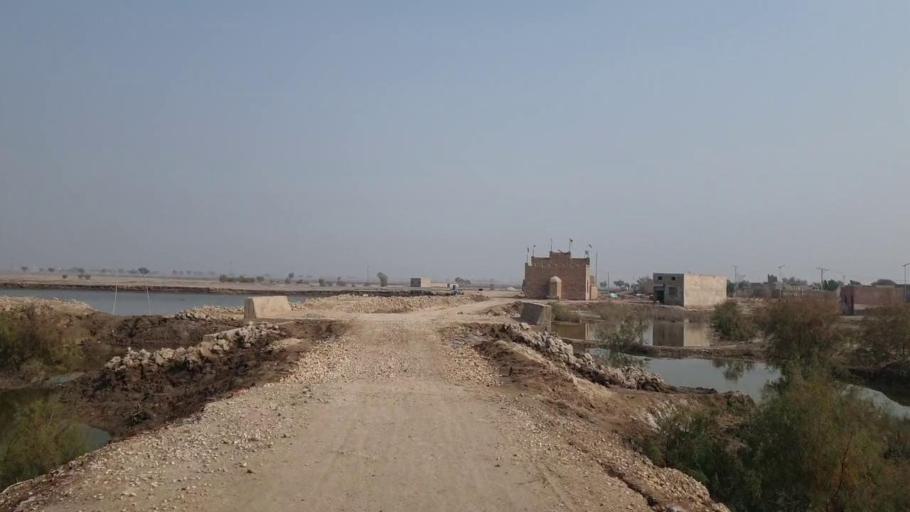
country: PK
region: Sindh
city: Bhan
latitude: 26.4564
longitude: 67.6927
